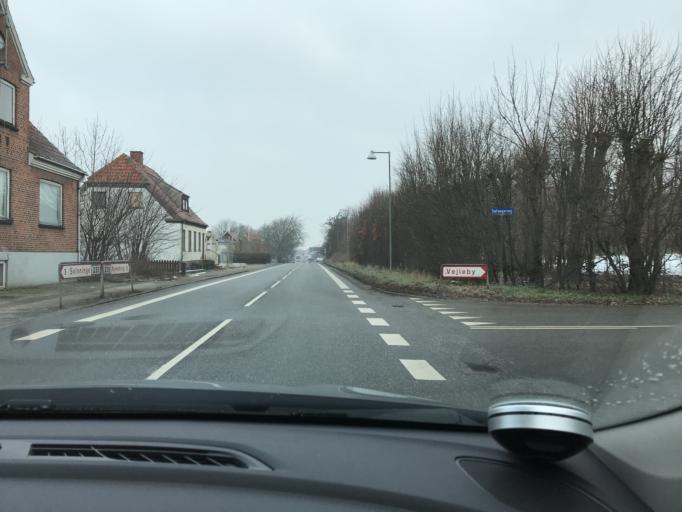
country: DK
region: Zealand
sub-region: Odsherred Kommune
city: Horve
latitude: 55.7471
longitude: 11.4562
